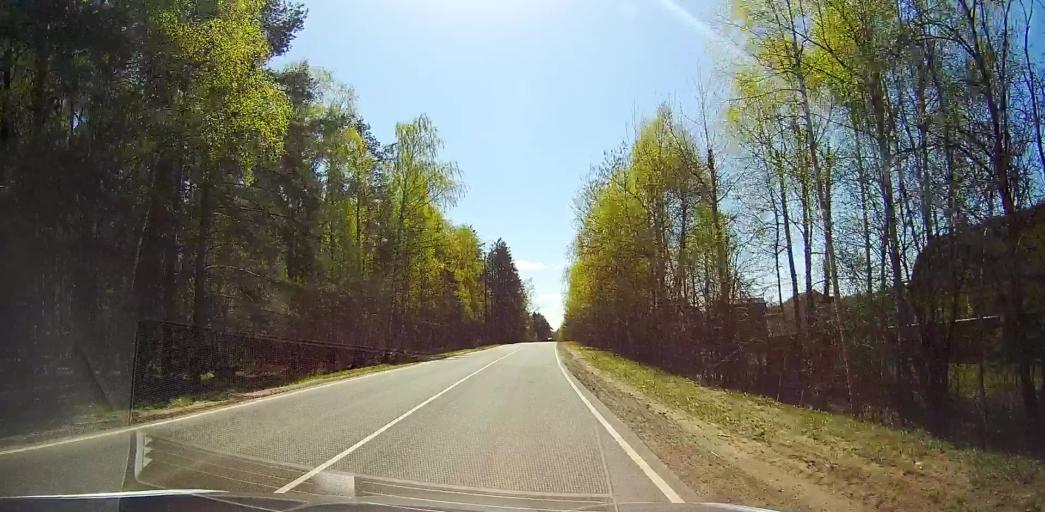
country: RU
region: Moskovskaya
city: Beloozerskiy
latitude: 55.4976
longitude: 38.4306
